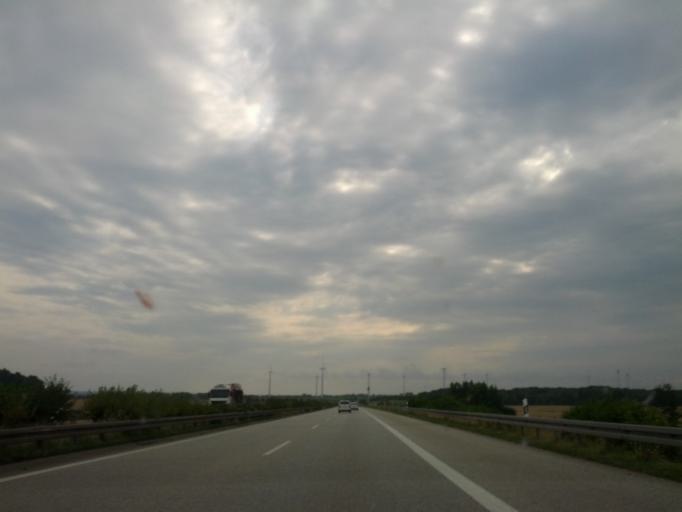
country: DE
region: Mecklenburg-Vorpommern
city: Jurgenshagen
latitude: 53.9822
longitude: 11.9214
